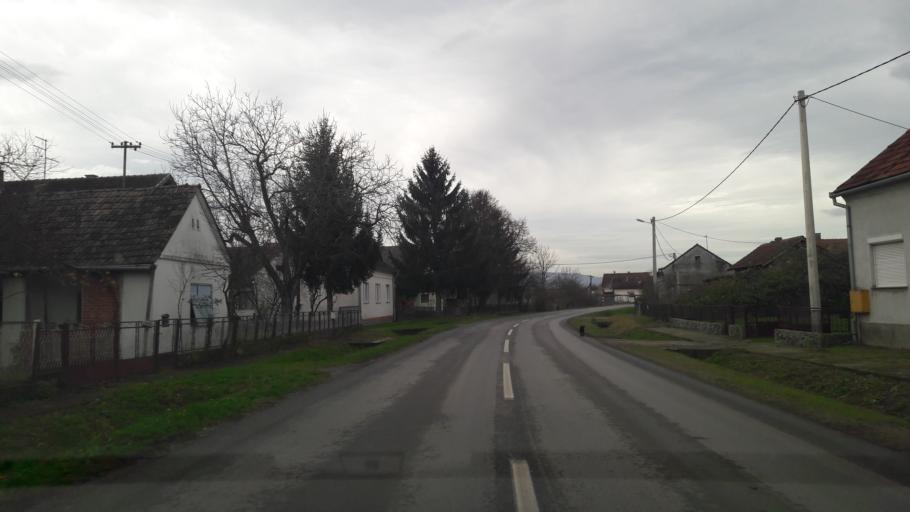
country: HR
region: Osjecko-Baranjska
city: Velimirovac
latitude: 45.5354
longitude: 18.0808
